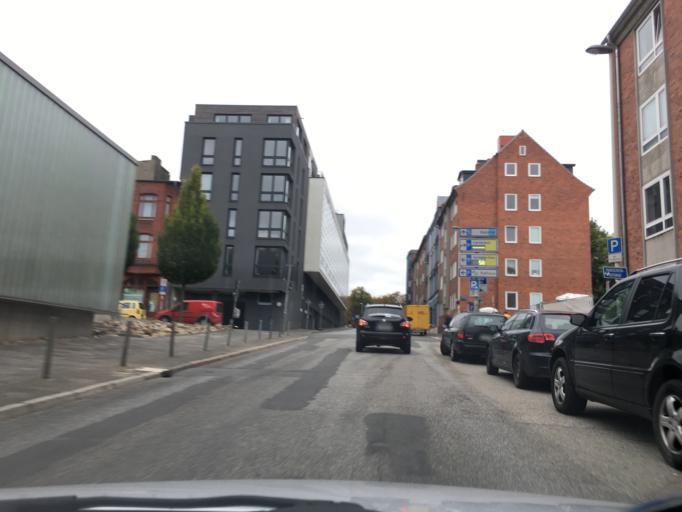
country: DE
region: Schleswig-Holstein
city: Kiel
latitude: 54.3225
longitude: 10.1310
